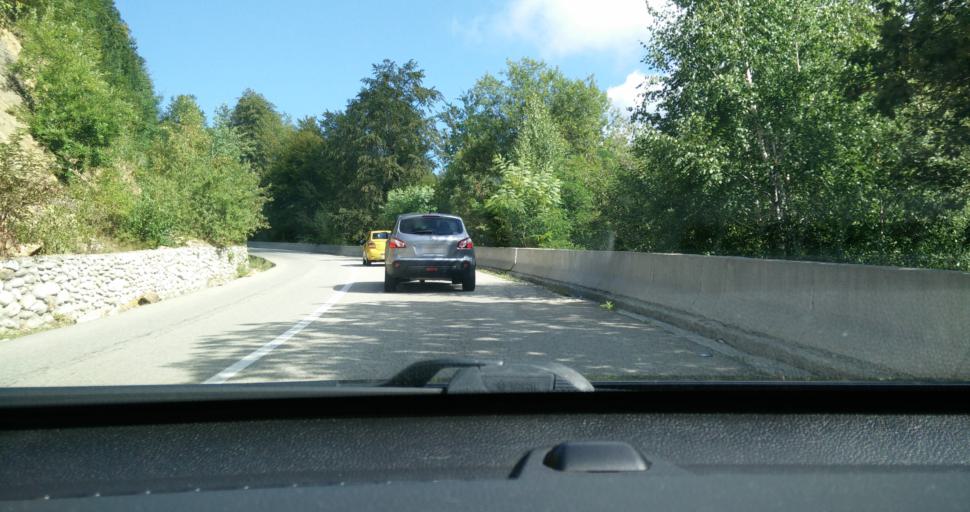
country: RO
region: Gorj
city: Novaci-Straini
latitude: 45.2266
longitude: 23.6947
